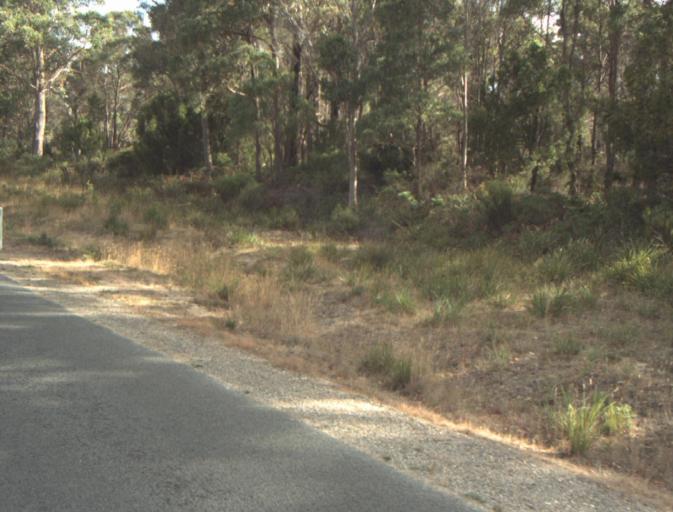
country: AU
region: Tasmania
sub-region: Dorset
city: Bridport
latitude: -41.1292
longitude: 147.2131
